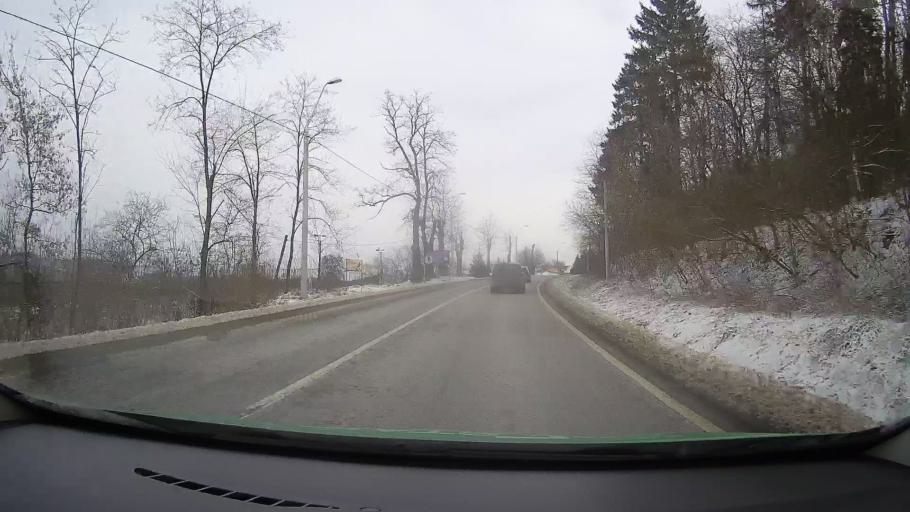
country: RO
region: Sibiu
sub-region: Comuna Darlos
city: Darlos
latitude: 46.1727
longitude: 24.3877
